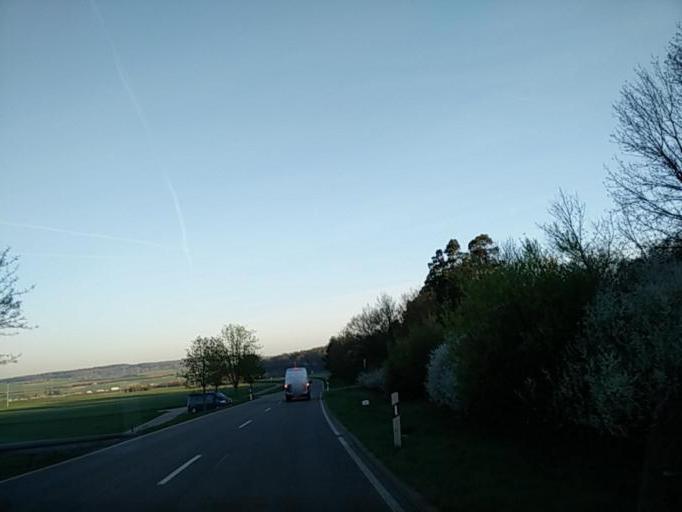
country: DE
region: Baden-Wuerttemberg
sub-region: Regierungsbezirk Stuttgart
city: Hildrizhausen
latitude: 48.6363
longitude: 8.9487
